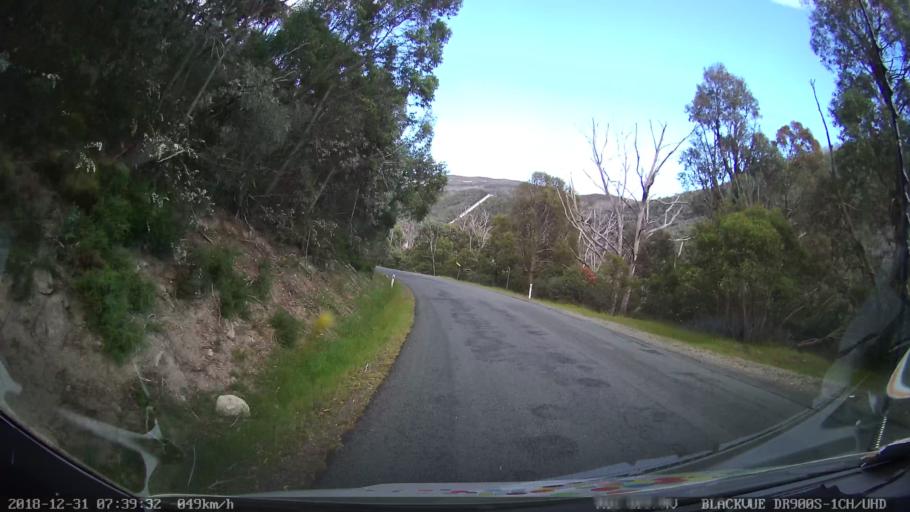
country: AU
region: New South Wales
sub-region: Snowy River
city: Jindabyne
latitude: -36.3493
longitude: 148.4206
